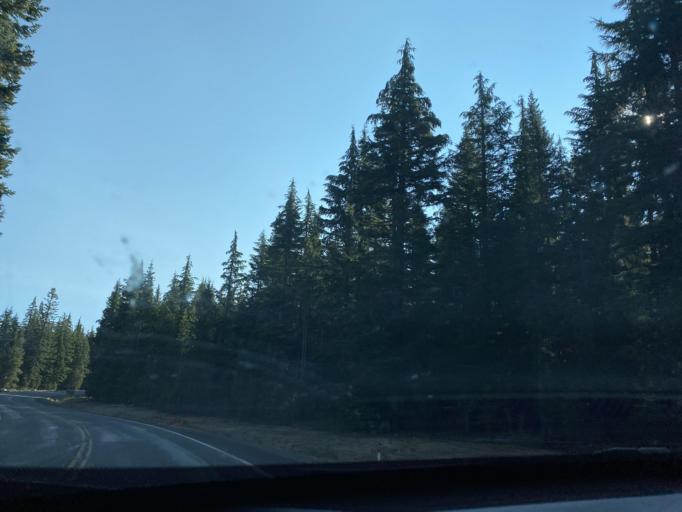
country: US
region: Oregon
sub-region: Deschutes County
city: Three Rivers
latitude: 43.7102
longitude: -121.2831
